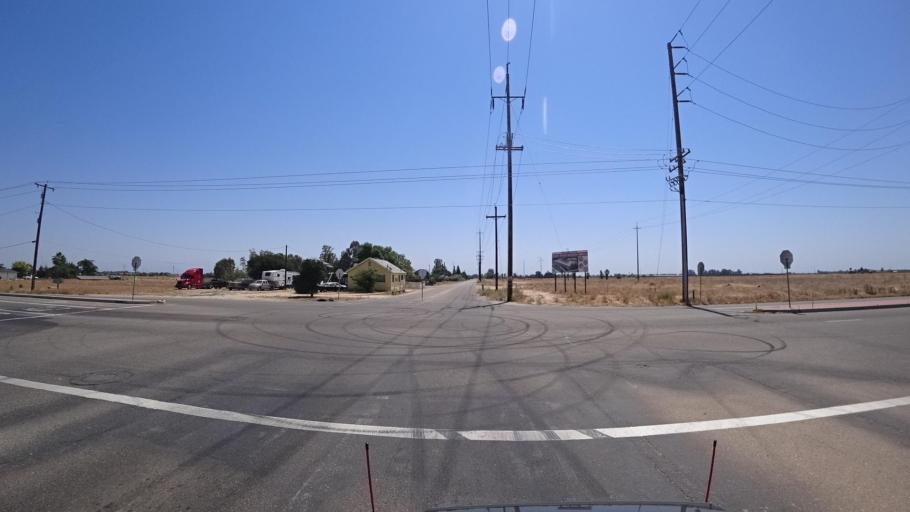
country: US
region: California
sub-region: Fresno County
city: Sunnyside
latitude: 36.7148
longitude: -119.6823
